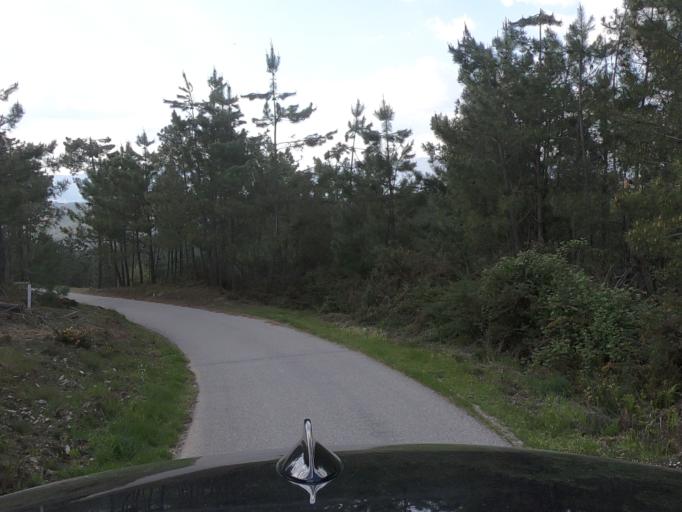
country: PT
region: Vila Real
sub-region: Sabrosa
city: Vilela
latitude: 41.2376
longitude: -7.6695
